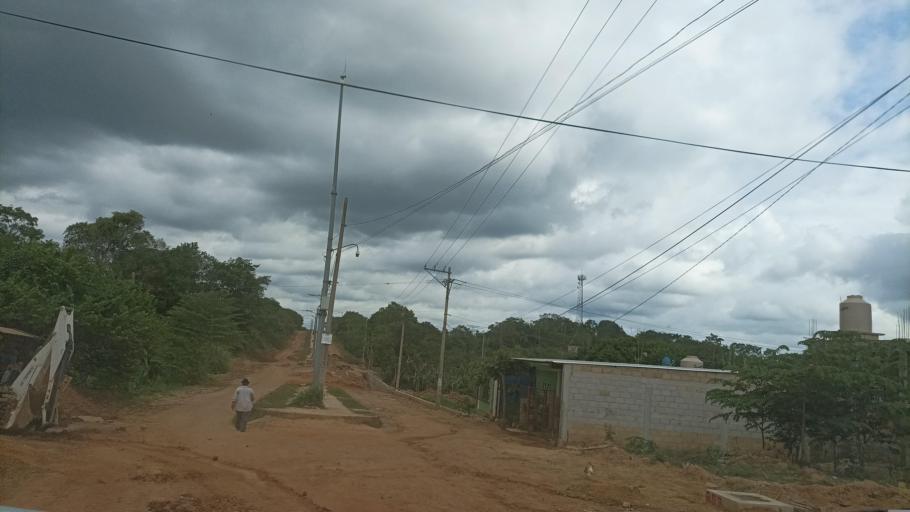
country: MX
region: Veracruz
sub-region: Soconusco
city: Colonia Lealtad
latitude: 17.9637
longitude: -94.8948
